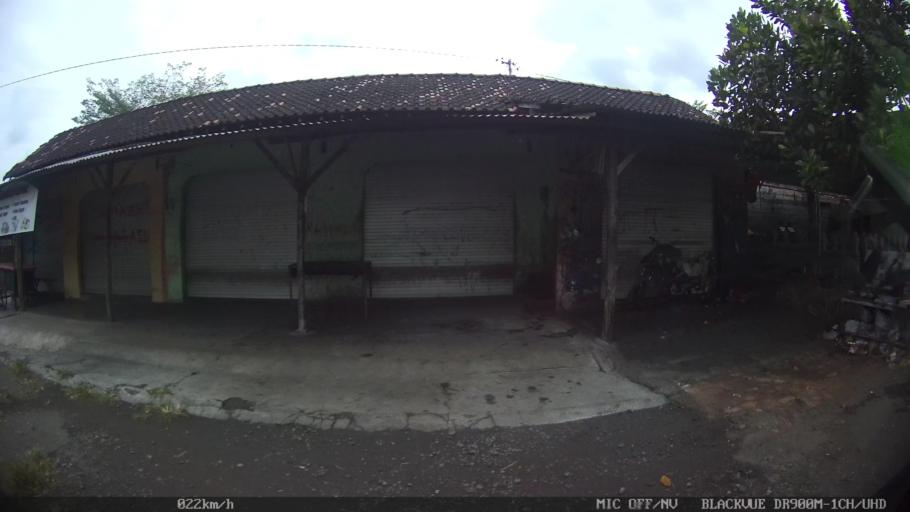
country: ID
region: Daerah Istimewa Yogyakarta
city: Sewon
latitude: -7.8759
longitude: 110.4070
